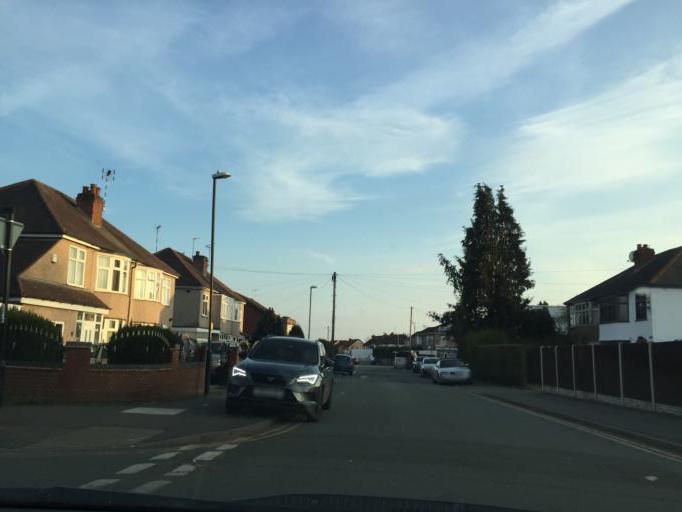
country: GB
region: England
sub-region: Coventry
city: Coventry
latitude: 52.4069
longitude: -1.5658
